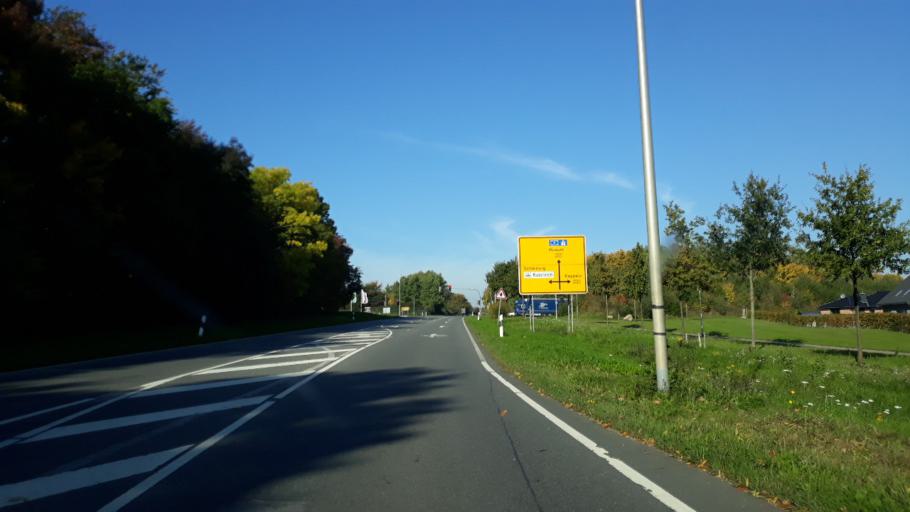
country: DE
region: Schleswig-Holstein
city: Schleswig
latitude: 54.5337
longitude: 9.5615
